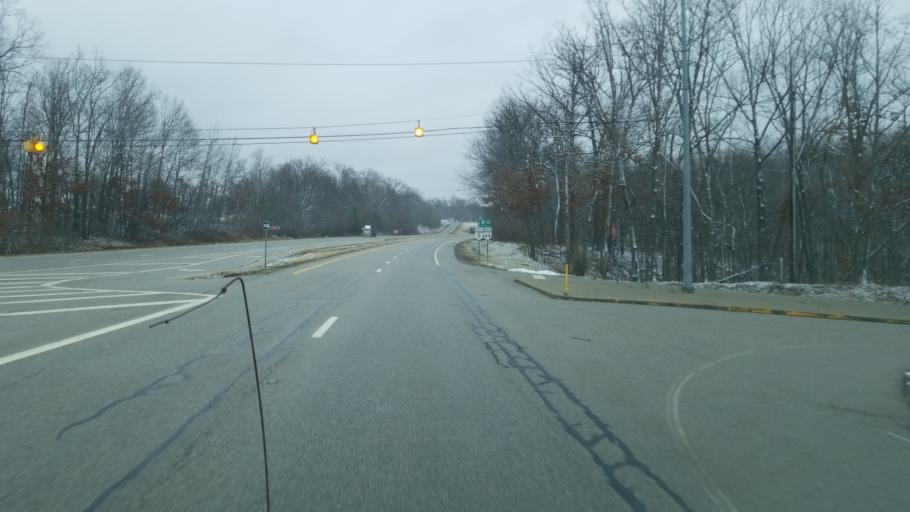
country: US
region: Ohio
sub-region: Portage County
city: Ravenna
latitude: 41.1489
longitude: -81.2210
